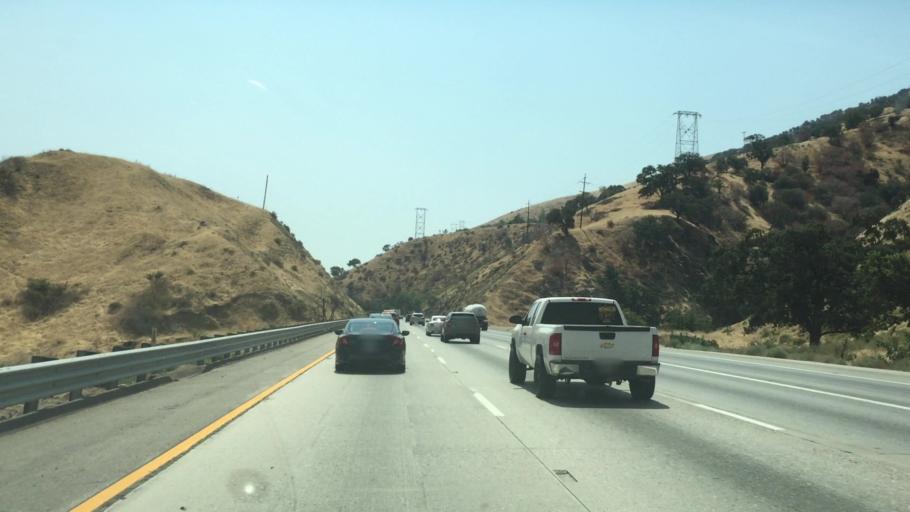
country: US
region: California
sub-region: Kern County
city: Lebec
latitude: 34.8937
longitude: -118.9182
